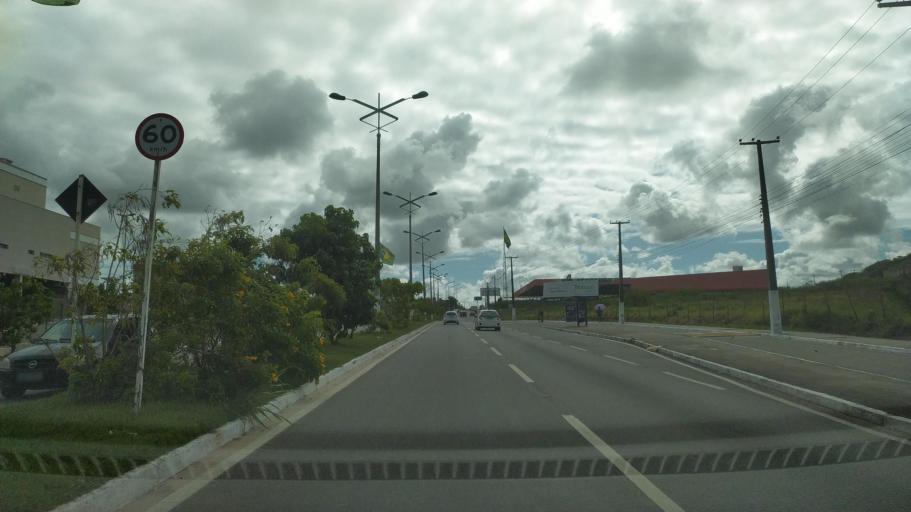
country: BR
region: Alagoas
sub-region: Maceio
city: Maceio
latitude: -9.6254
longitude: -35.6982
